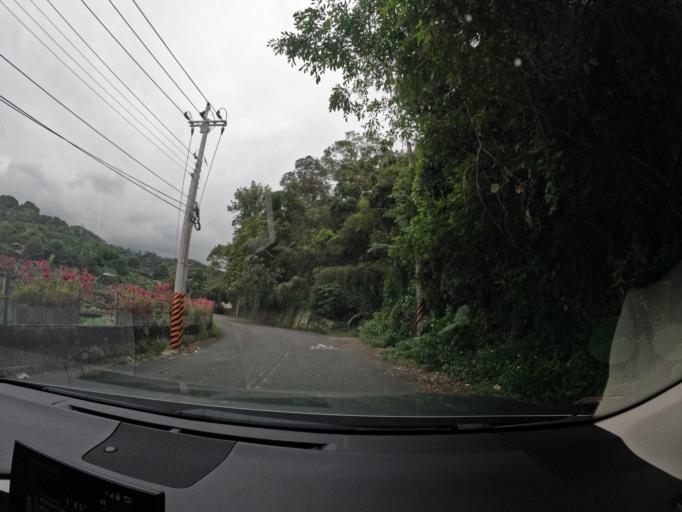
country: TW
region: Taiwan
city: Fengyuan
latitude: 24.3384
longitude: 120.8736
